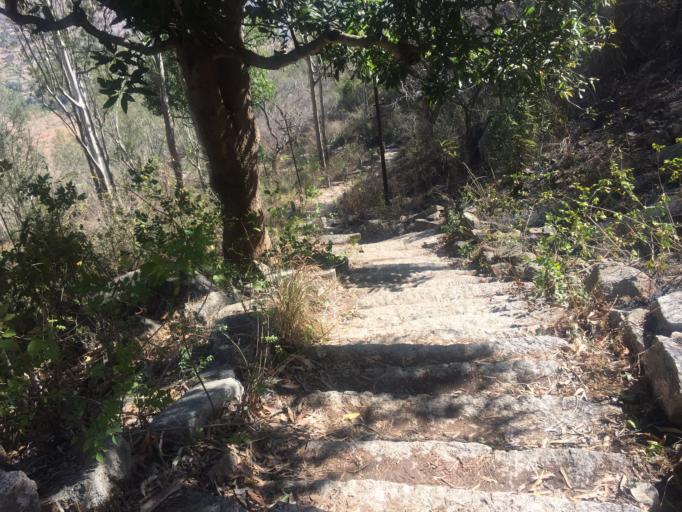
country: IN
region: Karnataka
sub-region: Chikkaballapur
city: Chik Ballapur
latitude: 13.3751
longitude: 77.6761
